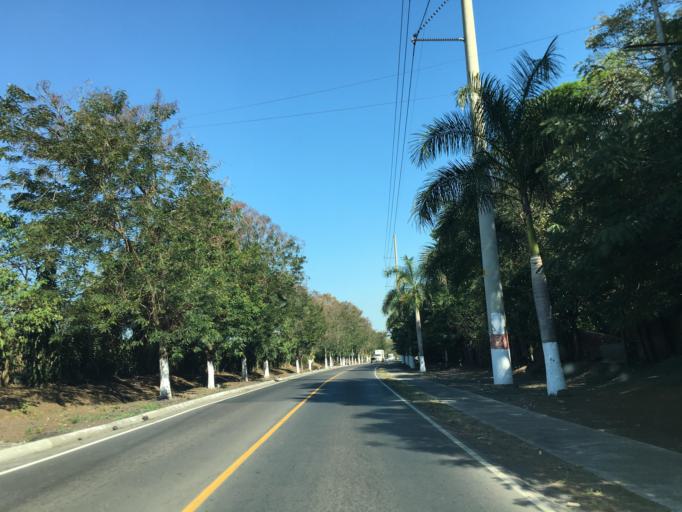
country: GT
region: Escuintla
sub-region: Municipio de La Democracia
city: La Democracia
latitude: 14.2389
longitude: -90.9548
